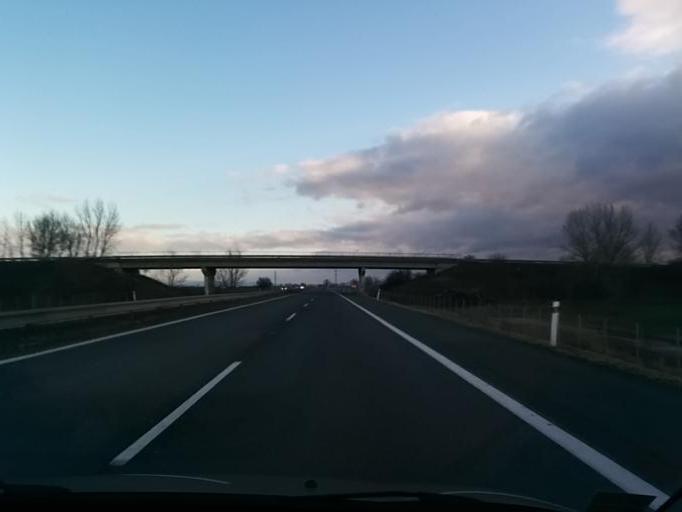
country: SK
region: Trnavsky
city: Leopoldov
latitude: 48.5199
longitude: 17.7763
